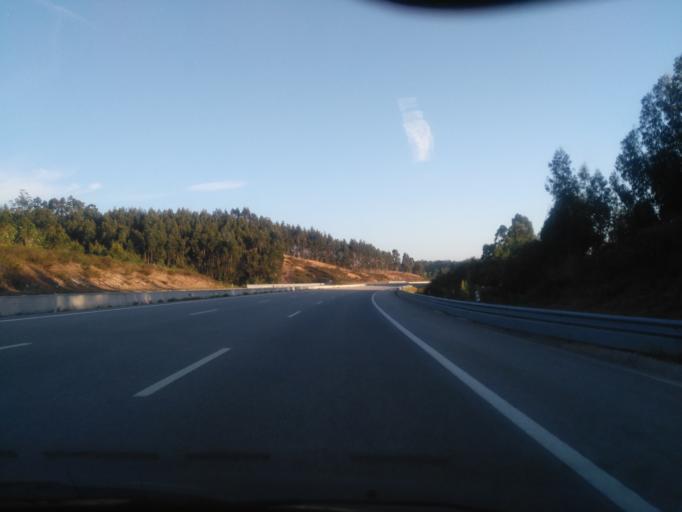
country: PT
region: Coimbra
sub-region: Figueira da Foz
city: Alhadas
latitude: 40.1335
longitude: -8.7443
